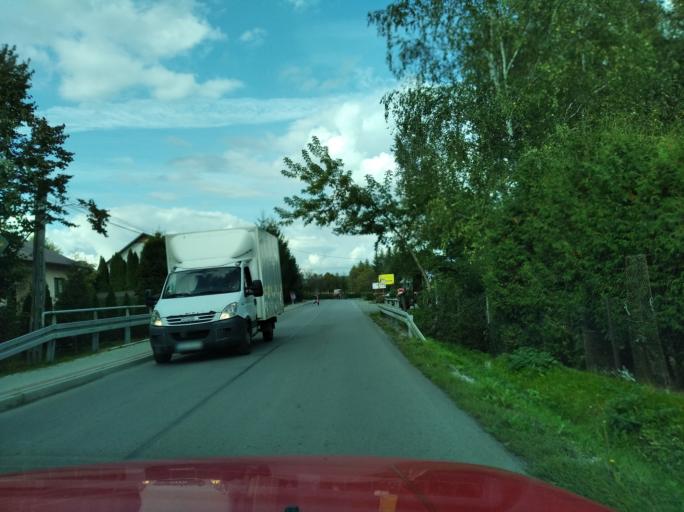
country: PL
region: Subcarpathian Voivodeship
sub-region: Powiat rzeszowski
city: Tyczyn
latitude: 49.9525
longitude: 22.0275
